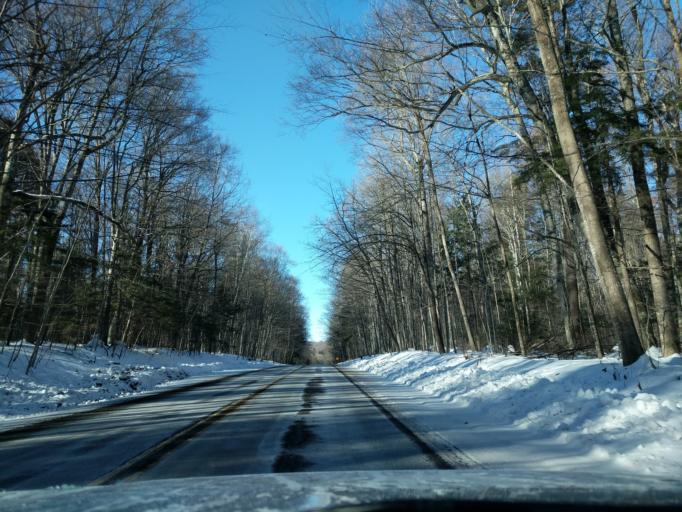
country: US
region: Wisconsin
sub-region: Menominee County
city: Keshena
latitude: 45.0906
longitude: -88.6290
